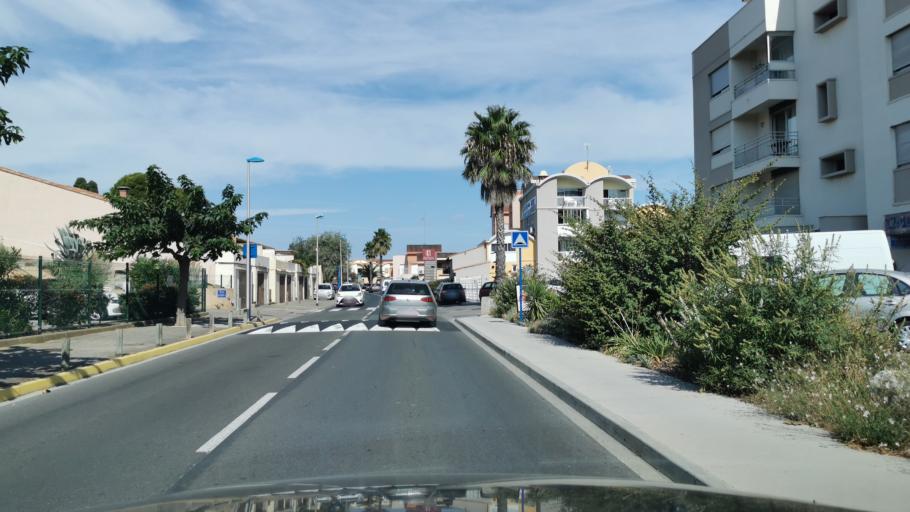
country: FR
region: Languedoc-Roussillon
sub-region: Departement de l'Aude
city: Gruissan
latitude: 43.1077
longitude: 3.0950
